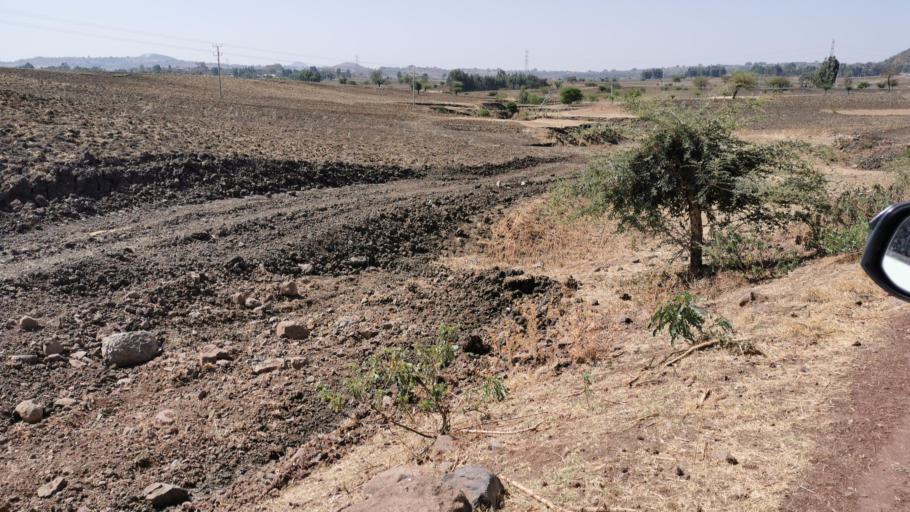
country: ET
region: Amhara
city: Bahir Dar
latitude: 11.8375
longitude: 37.0013
